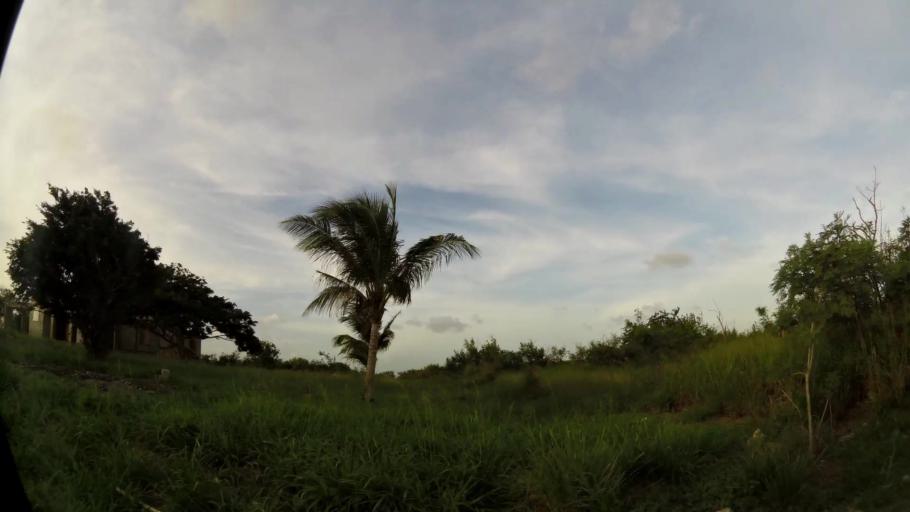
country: BB
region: Christ Church
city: Oistins
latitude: 13.0875
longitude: -59.4942
